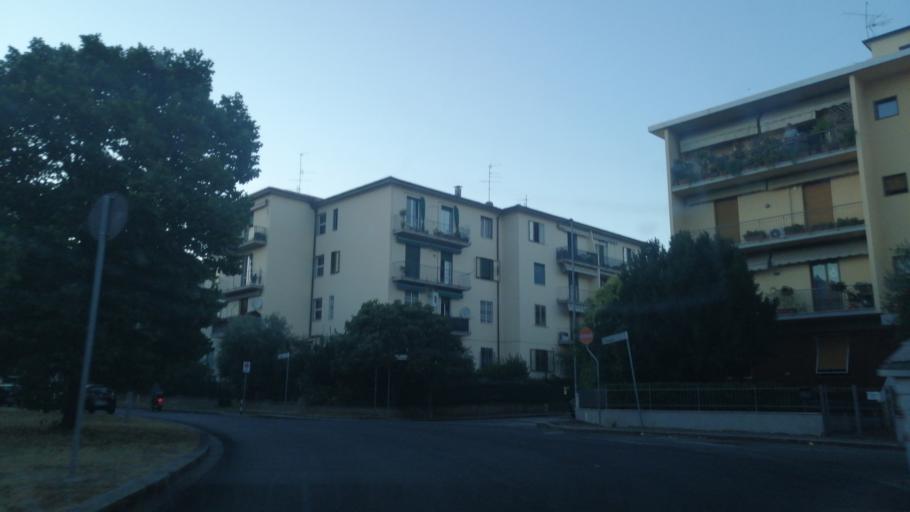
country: IT
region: Tuscany
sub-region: Province of Florence
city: Sesto Fiorentino
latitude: 43.8363
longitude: 11.2082
